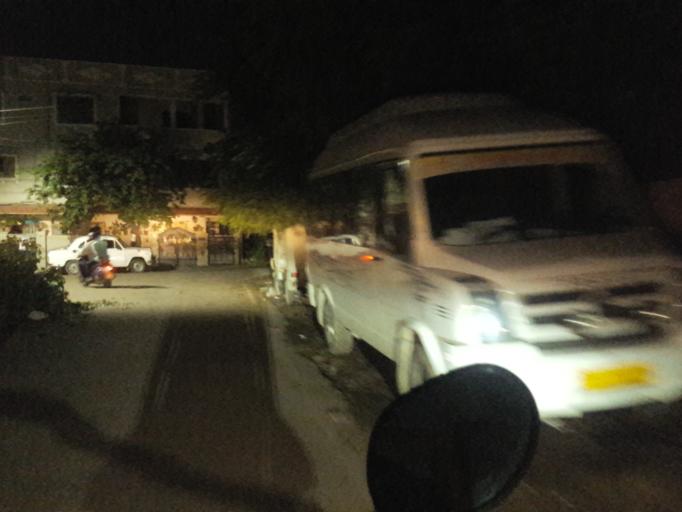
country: IN
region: Telangana
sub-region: Rangareddi
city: Kukatpalli
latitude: 17.4849
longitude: 78.3925
